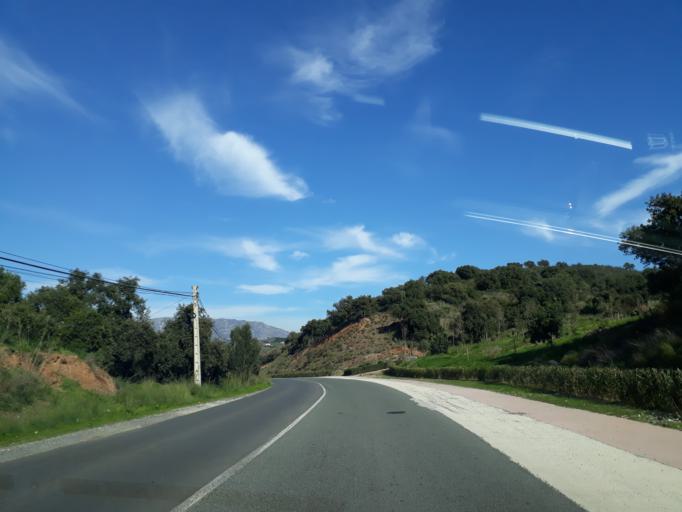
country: ES
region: Andalusia
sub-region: Provincia de Malaga
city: Fuengirola
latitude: 36.5123
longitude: -4.6876
